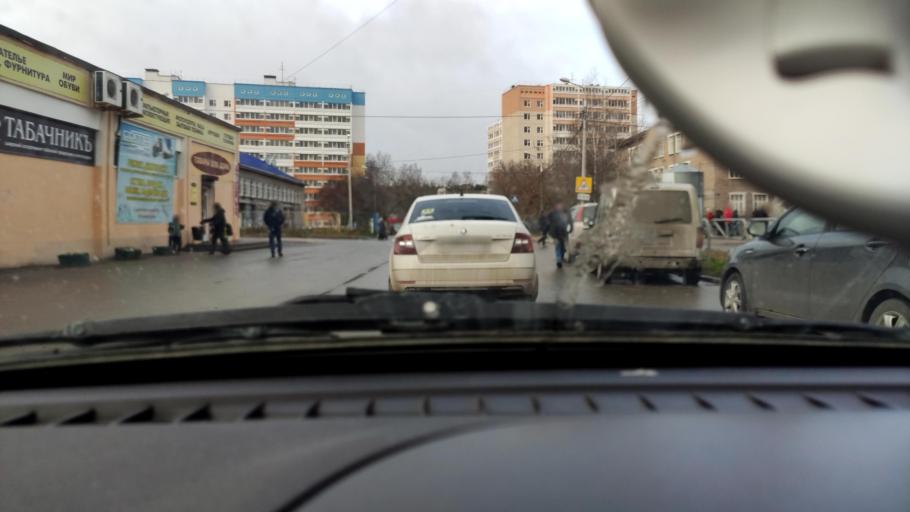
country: RU
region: Perm
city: Kondratovo
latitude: 58.0374
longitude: 56.1327
